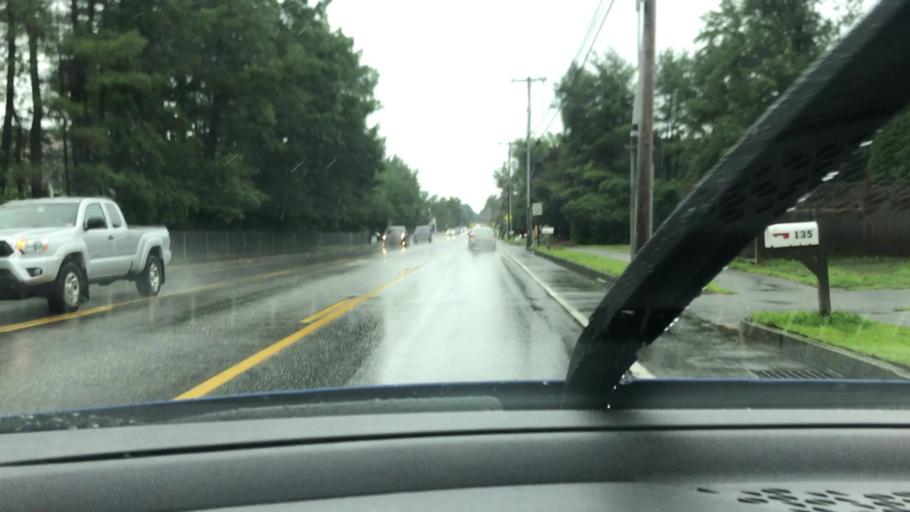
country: US
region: New Hampshire
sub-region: Merrimack County
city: East Concord
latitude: 43.2613
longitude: -71.5823
